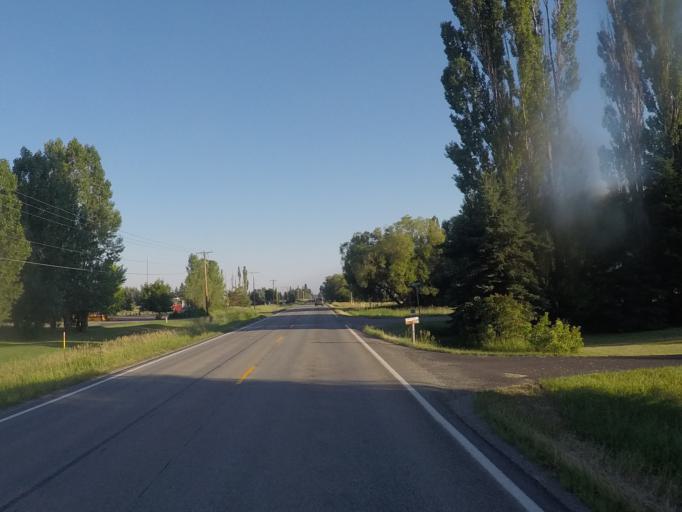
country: US
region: Montana
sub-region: Flathead County
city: Columbia Falls
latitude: 48.3380
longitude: -114.1594
